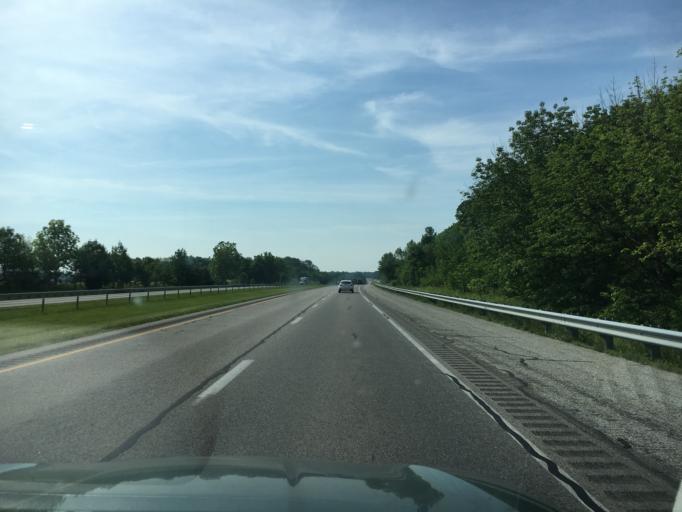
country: US
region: Indiana
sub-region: Decatur County
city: Saint Paul
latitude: 39.4299
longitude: -85.5834
